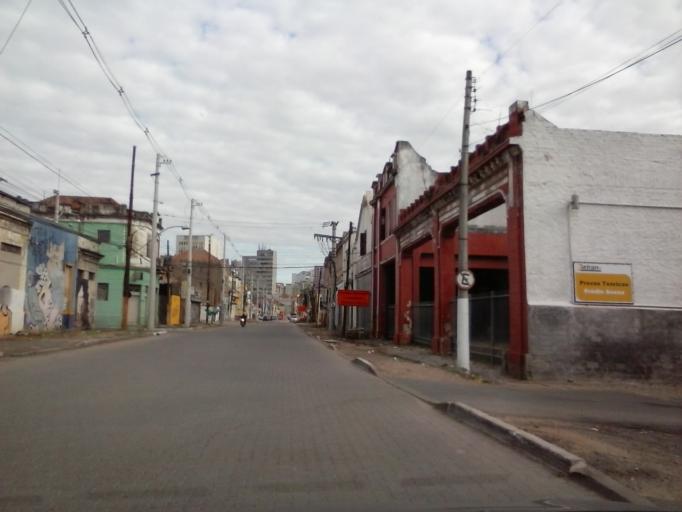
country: BR
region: Rio Grande do Sul
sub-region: Porto Alegre
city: Porto Alegre
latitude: -30.0223
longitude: -51.2156
